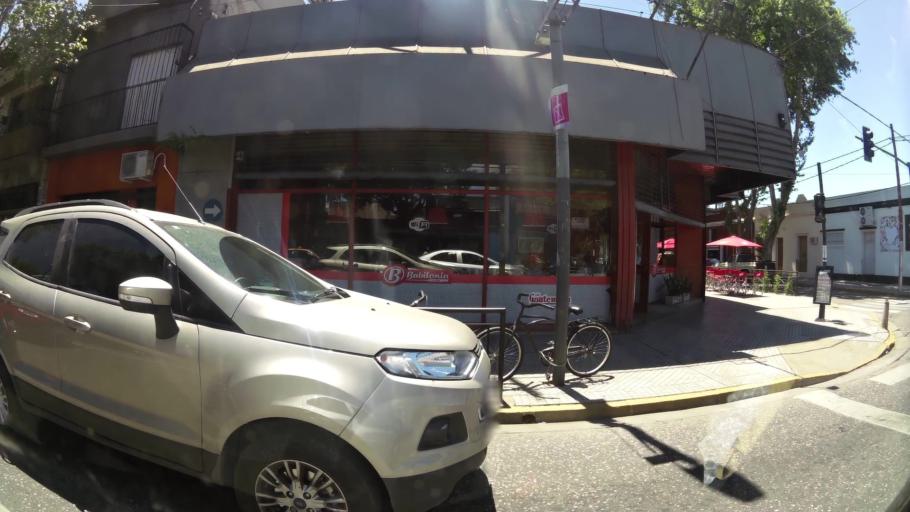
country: AR
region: Santa Fe
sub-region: Departamento de Rosario
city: Rosario
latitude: -32.9439
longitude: -60.6819
